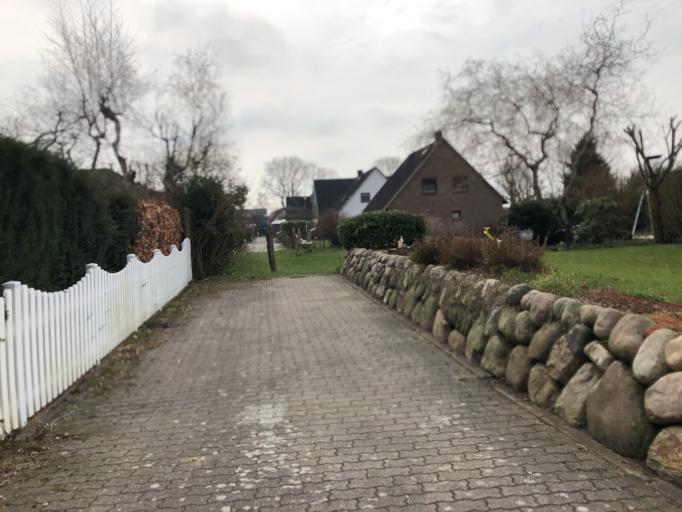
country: DE
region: Schleswig-Holstein
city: Wanderup
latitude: 54.6860
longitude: 9.3304
